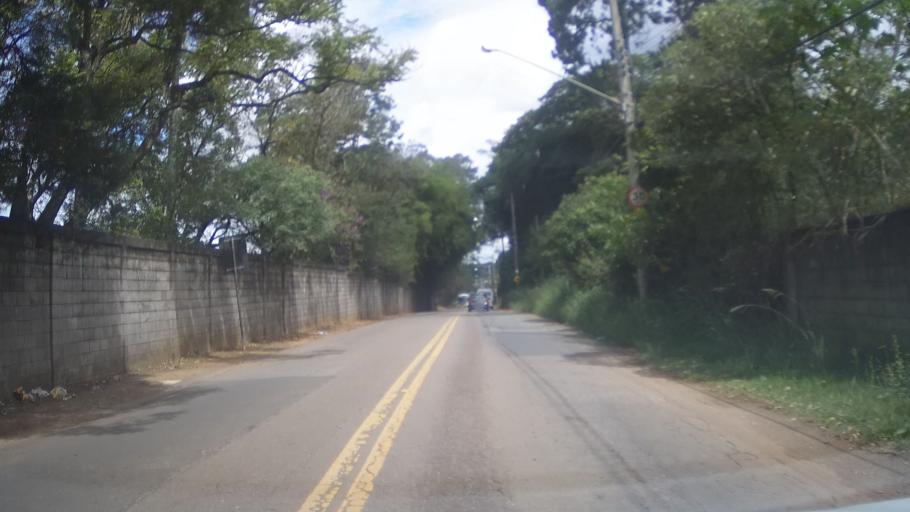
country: BR
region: Sao Paulo
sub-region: Varzea Paulista
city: Varzea Paulista
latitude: -23.1622
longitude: -46.8280
